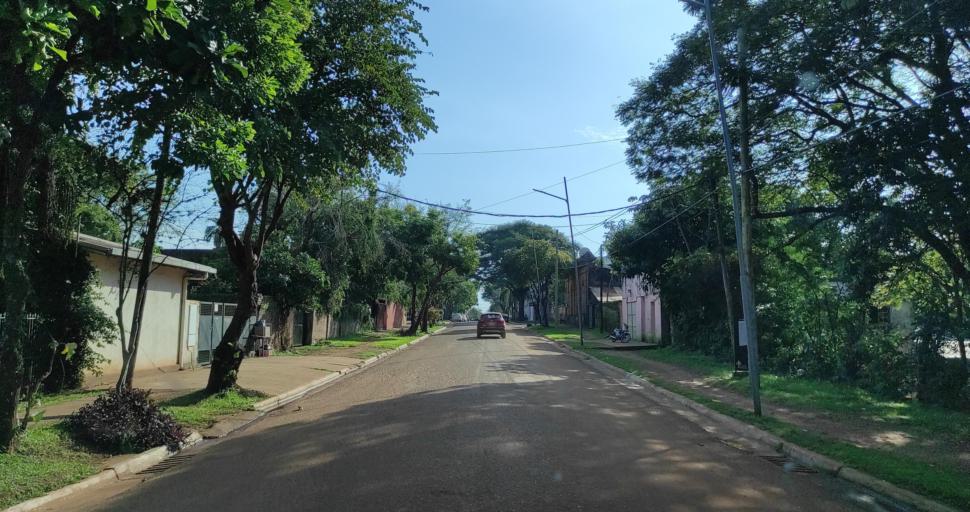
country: AR
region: Corrientes
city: Santo Tome
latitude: -28.5498
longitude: -56.0330
